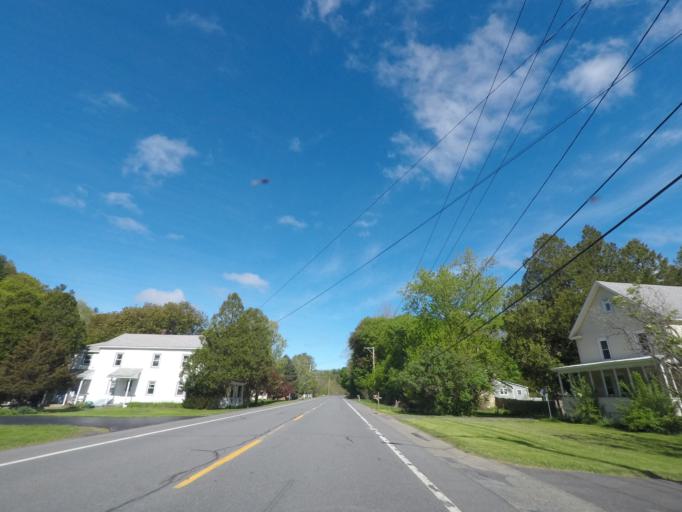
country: US
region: New York
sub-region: Albany County
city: Ravena
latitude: 42.4738
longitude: -73.9012
